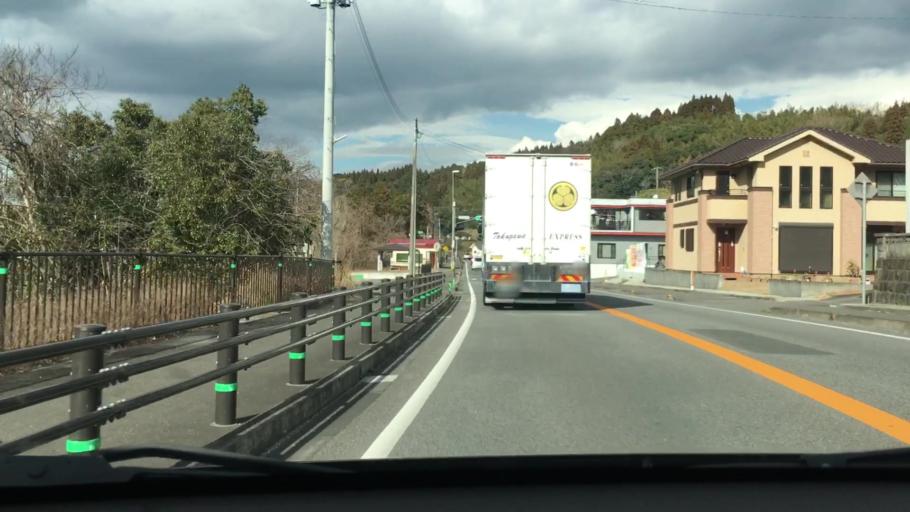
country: JP
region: Oita
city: Usuki
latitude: 33.0446
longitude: 131.6919
